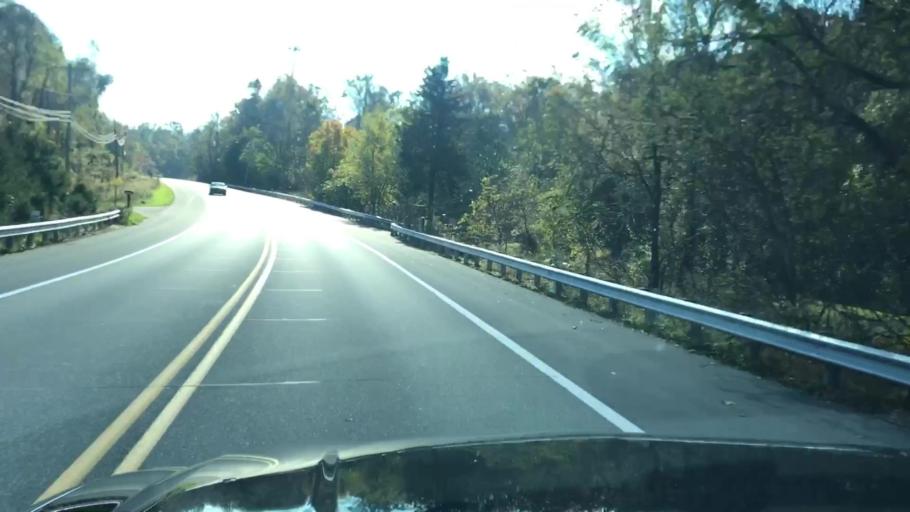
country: US
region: Pennsylvania
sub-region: Cumberland County
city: Lower Allen
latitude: 40.1685
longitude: -76.8890
